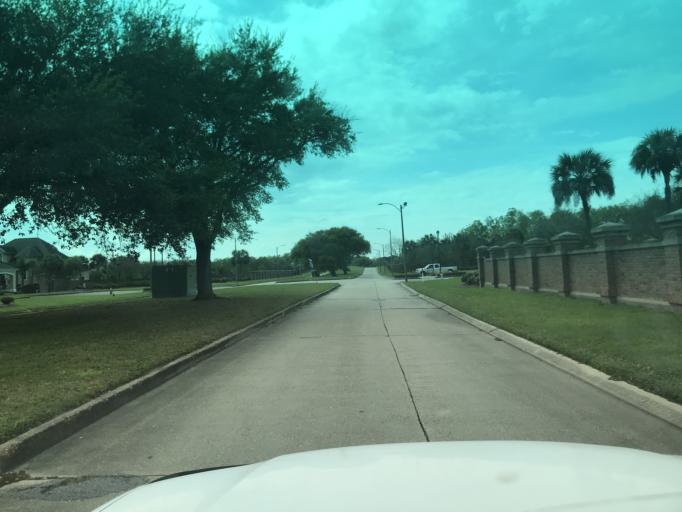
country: US
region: Louisiana
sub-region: Saint Bernard Parish
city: Chalmette
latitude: 30.0394
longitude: -89.9465
